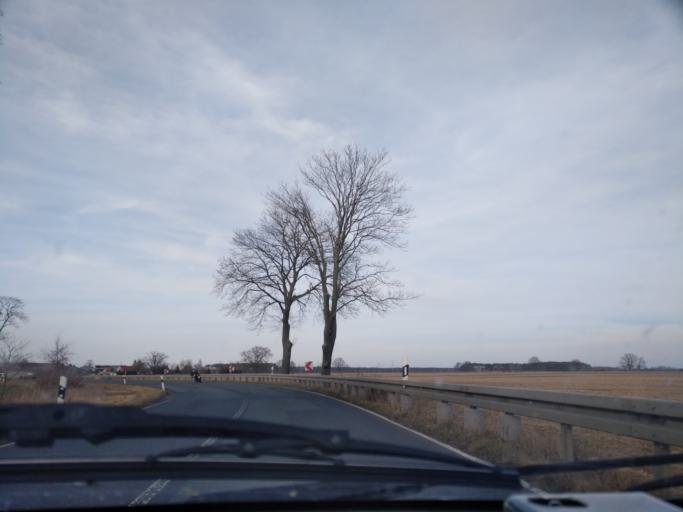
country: DE
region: Saxony-Anhalt
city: Holzdorf
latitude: 51.8139
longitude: 13.1648
